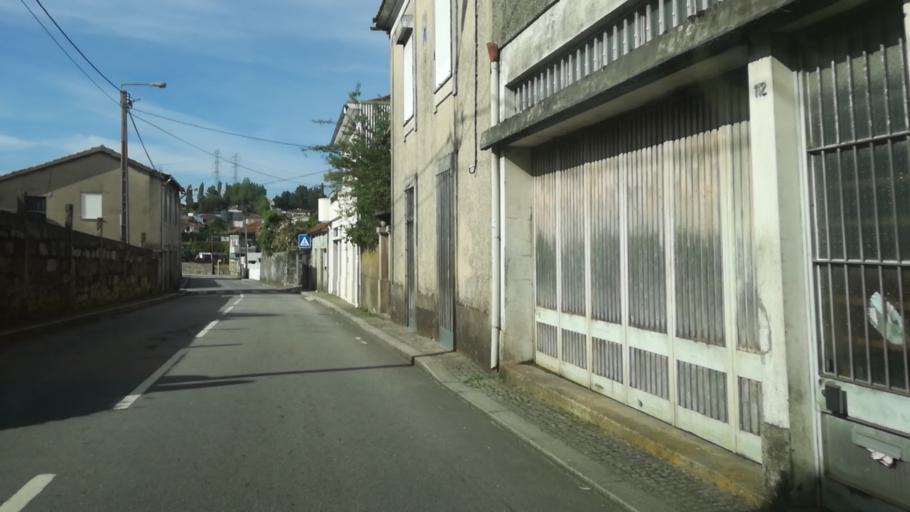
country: PT
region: Porto
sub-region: Maia
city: Nogueira
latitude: 41.2308
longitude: -8.5873
